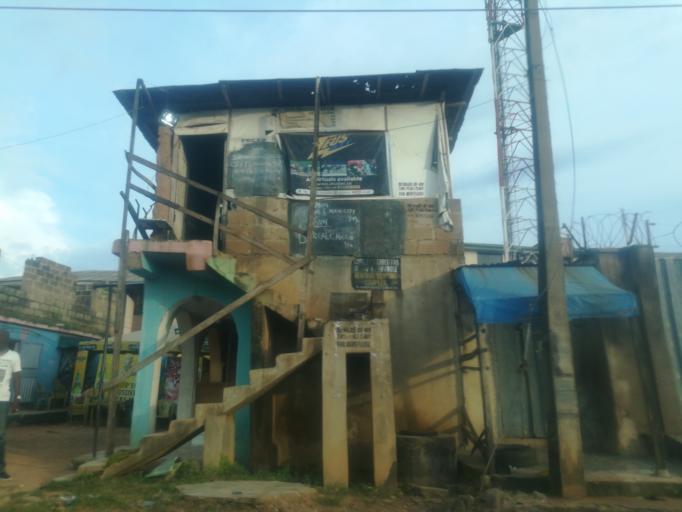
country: NG
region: Oyo
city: Ibadan
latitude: 7.3795
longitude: 3.8535
